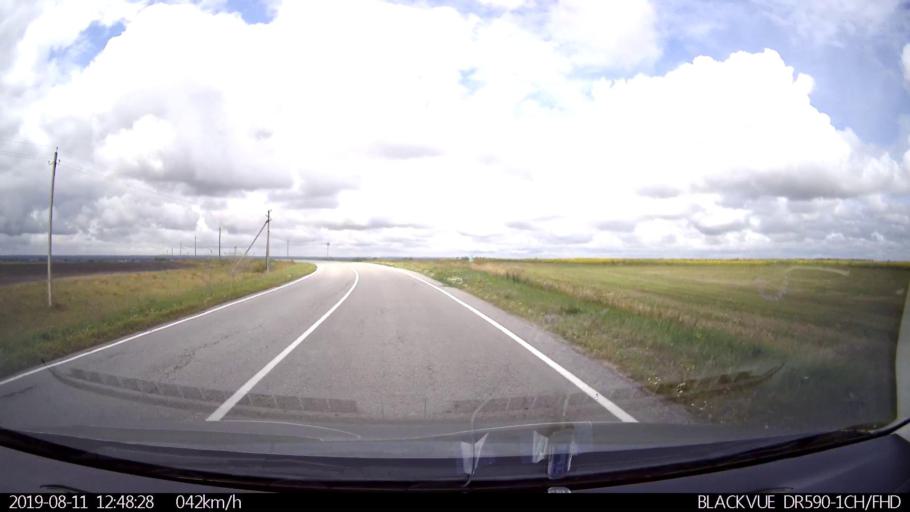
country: RU
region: Ulyanovsk
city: Ignatovka
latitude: 53.8739
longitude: 47.6990
